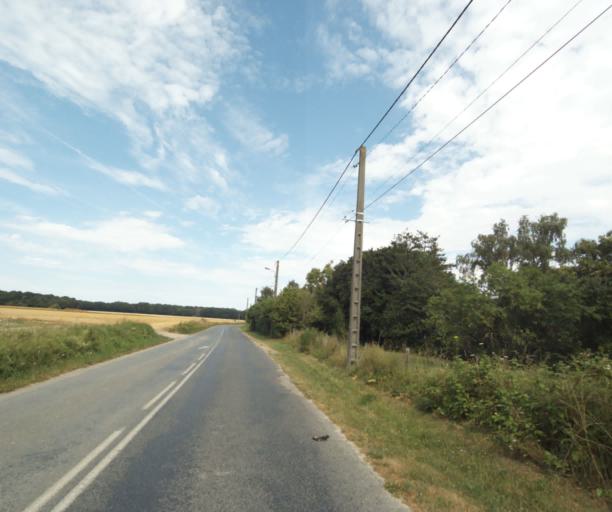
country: FR
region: Ile-de-France
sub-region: Departement de Seine-et-Marne
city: Chailly-en-Biere
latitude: 48.4740
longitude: 2.6159
